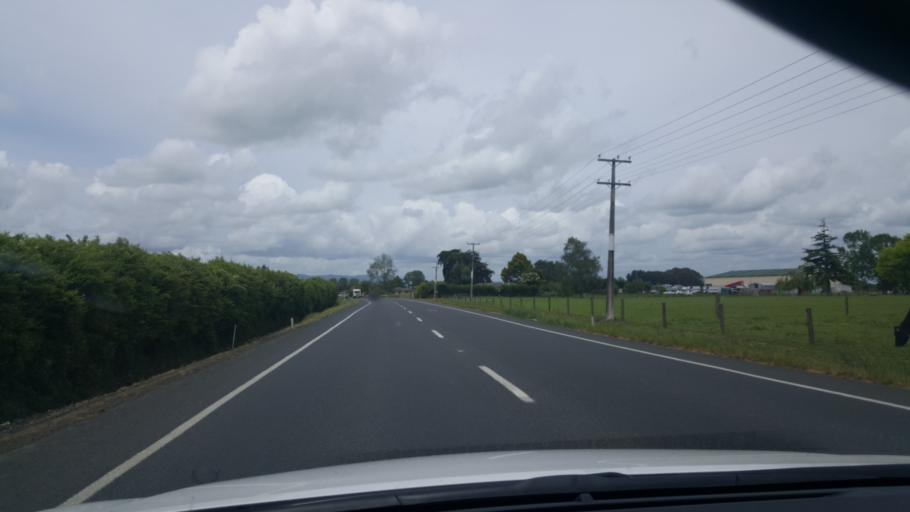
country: NZ
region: Waikato
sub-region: Matamata-Piako District
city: Matamata
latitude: -37.8848
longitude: 175.7652
